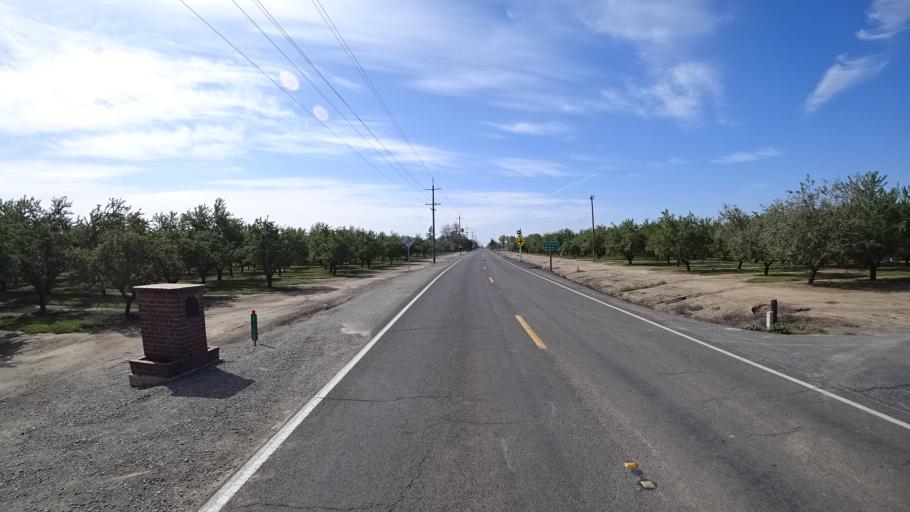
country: US
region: California
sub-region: Glenn County
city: Hamilton City
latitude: 39.6325
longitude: -122.0068
